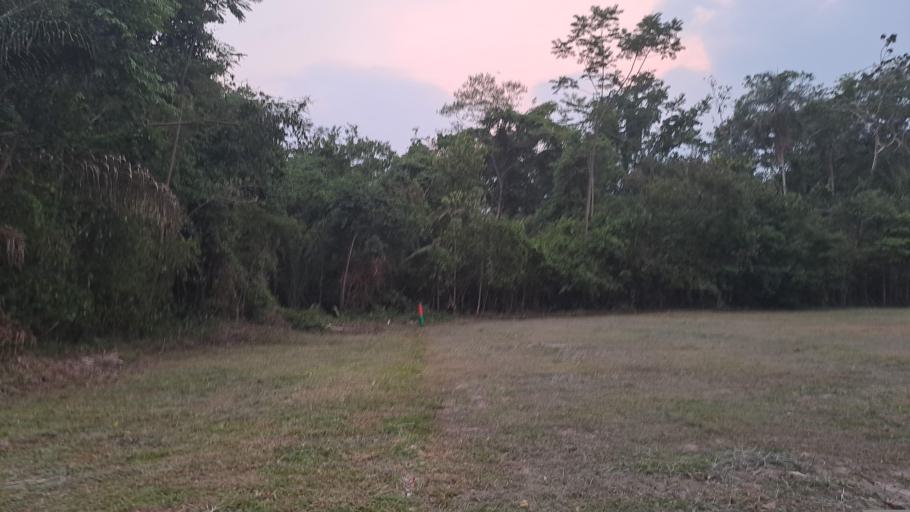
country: BO
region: La Paz
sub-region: Provincia Larecaja
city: Guanay
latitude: -15.5674
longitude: -67.3260
